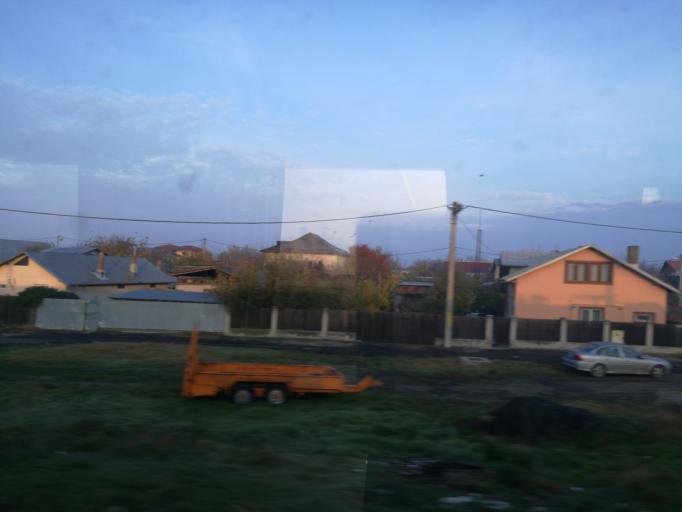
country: RO
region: Prahova
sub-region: Oras Mizil
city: Mizil
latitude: 45.0032
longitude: 26.4569
